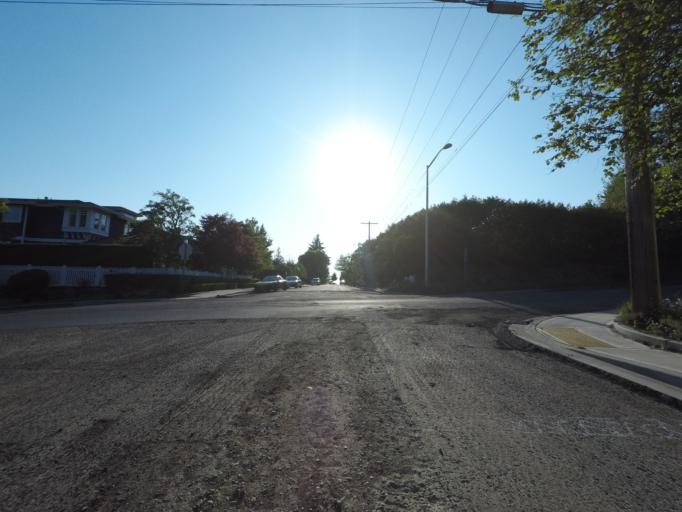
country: US
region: Washington
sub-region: King County
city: Kirkland
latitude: 47.6830
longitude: -122.2040
